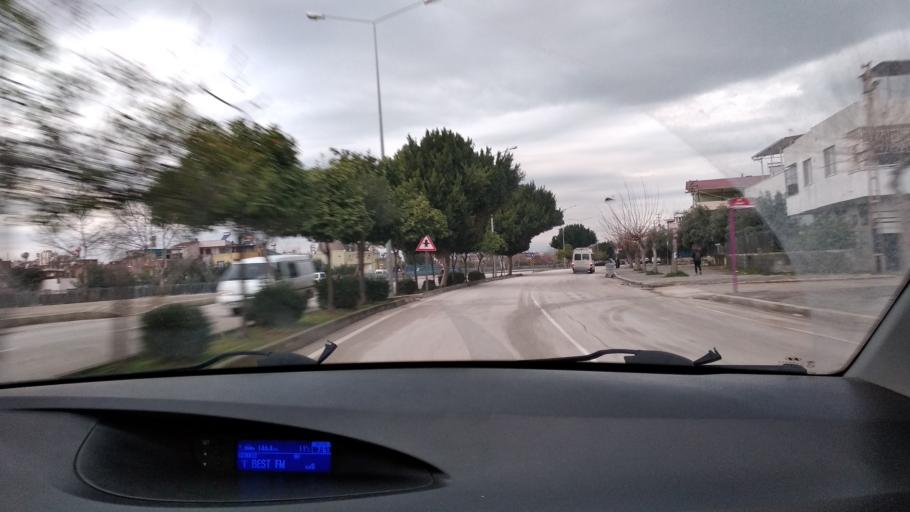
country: TR
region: Adana
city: Yuregir
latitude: 37.0111
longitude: 35.3888
